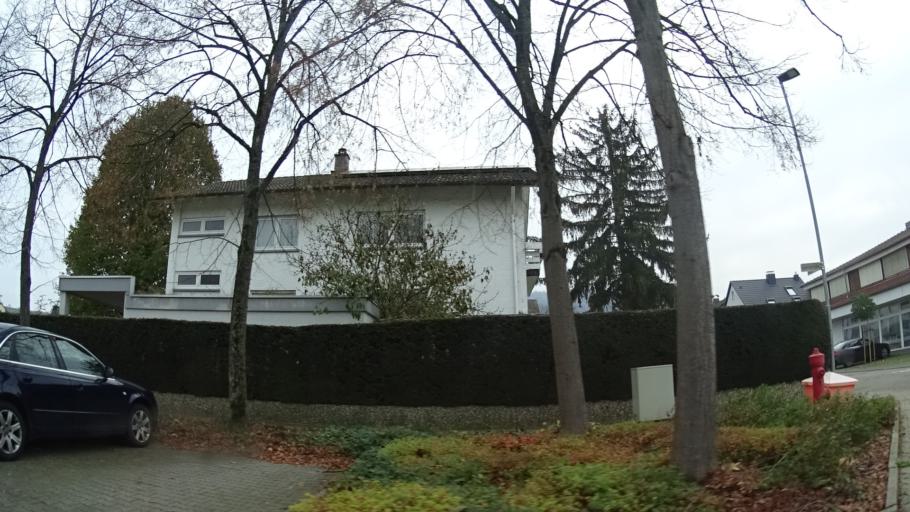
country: DE
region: Baden-Wuerttemberg
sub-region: Karlsruhe Region
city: Sinzheim
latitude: 48.7567
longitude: 8.1706
